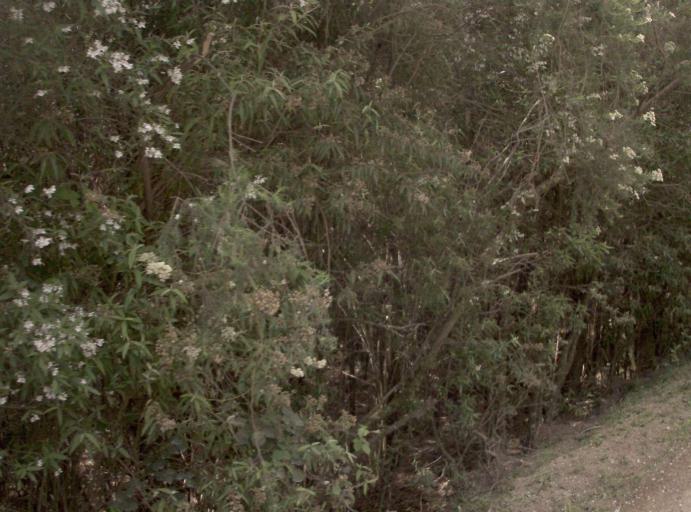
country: AU
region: Victoria
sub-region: Latrobe
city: Traralgon
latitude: -38.4114
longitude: 146.6213
